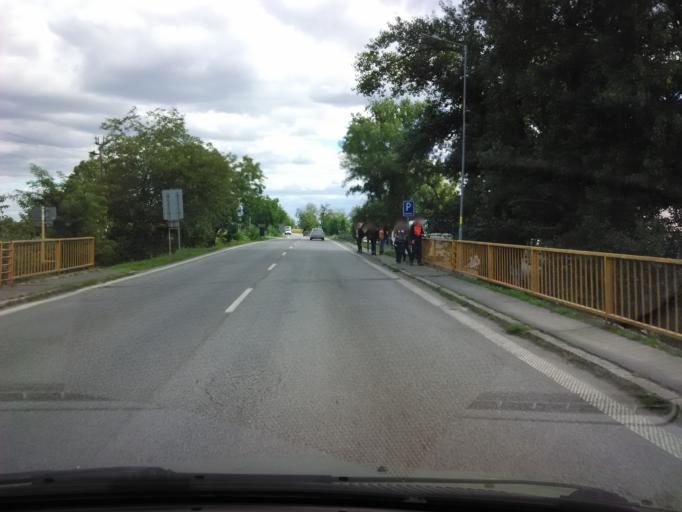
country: SK
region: Nitriansky
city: Levice
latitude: 48.2023
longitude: 18.5235
